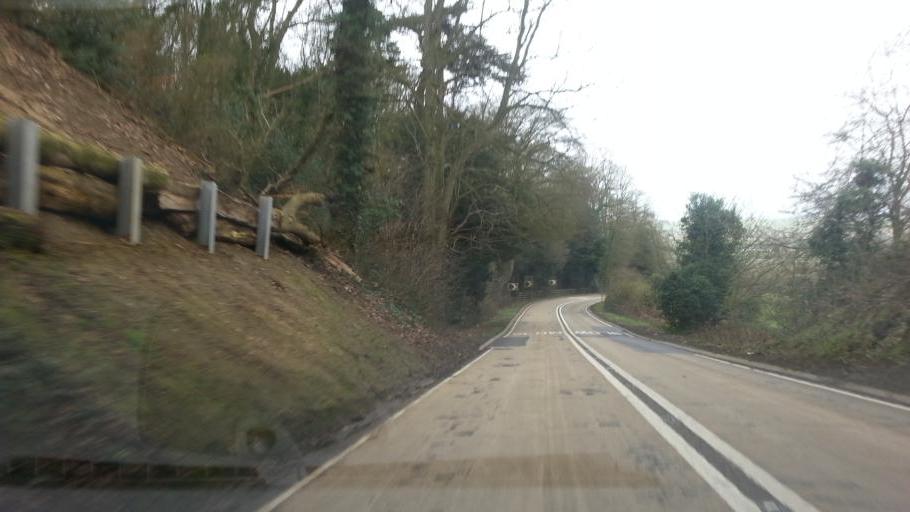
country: GB
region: England
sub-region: Leicestershire
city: Grimston
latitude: 52.8099
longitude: -0.9419
